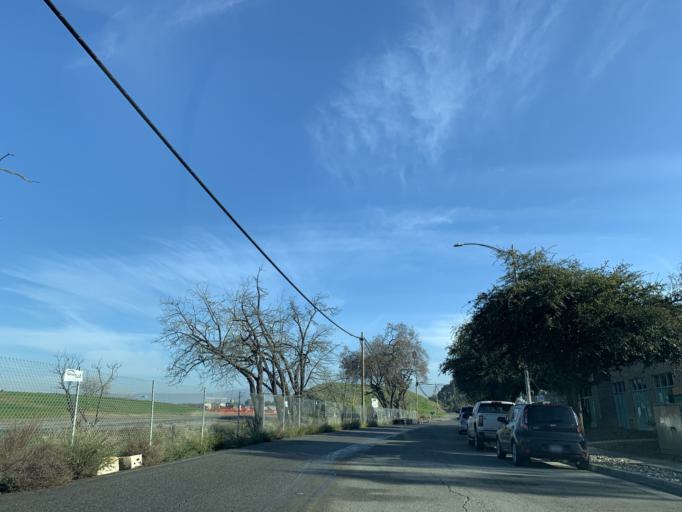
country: US
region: California
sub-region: Santa Clara County
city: Seven Trees
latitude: 37.2821
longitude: -121.8470
